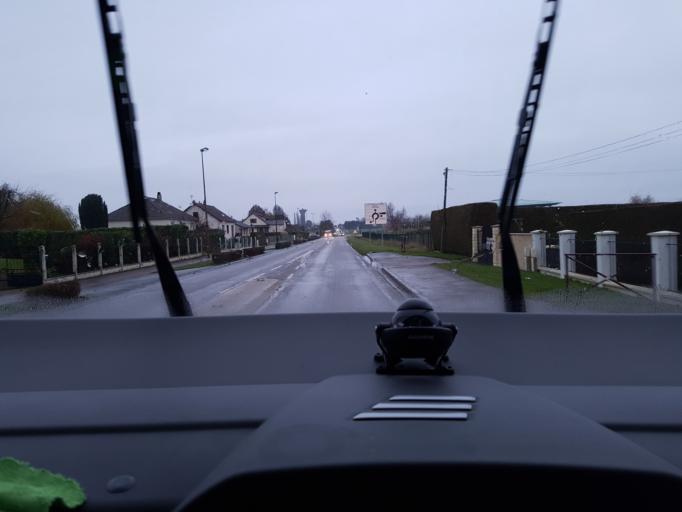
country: FR
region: Haute-Normandie
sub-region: Departement de l'Eure
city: Saint-Pierre-des-Fleurs
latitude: 49.2107
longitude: 0.9372
